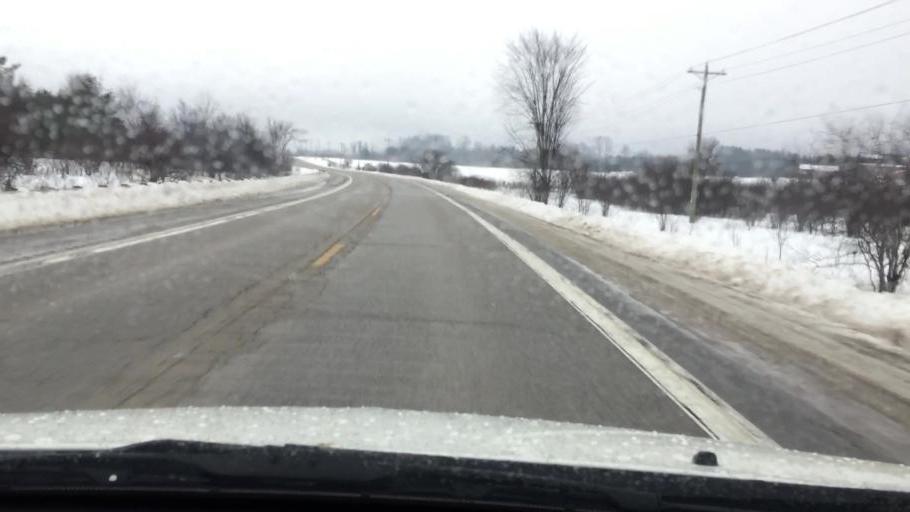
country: US
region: Michigan
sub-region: Charlevoix County
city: East Jordan
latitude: 45.1301
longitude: -85.1384
